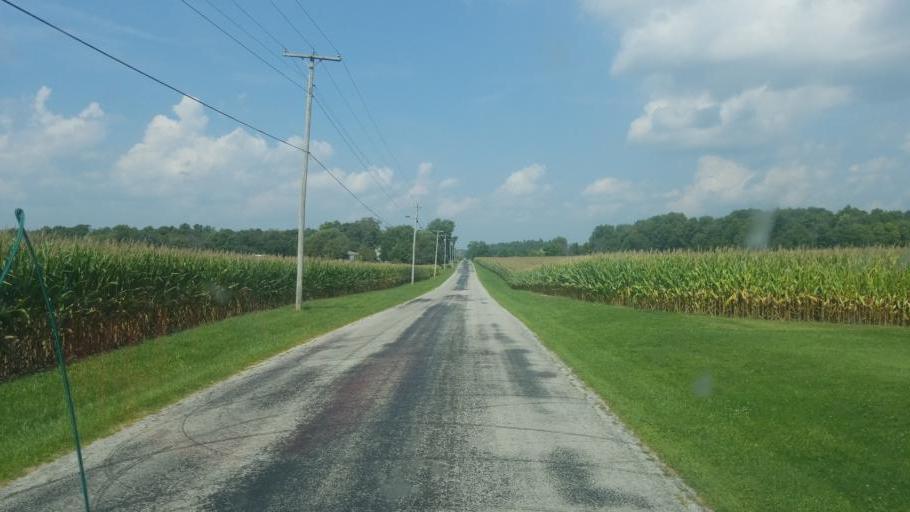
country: US
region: Ohio
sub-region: Richland County
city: Shelby
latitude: 40.8740
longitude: -82.5956
